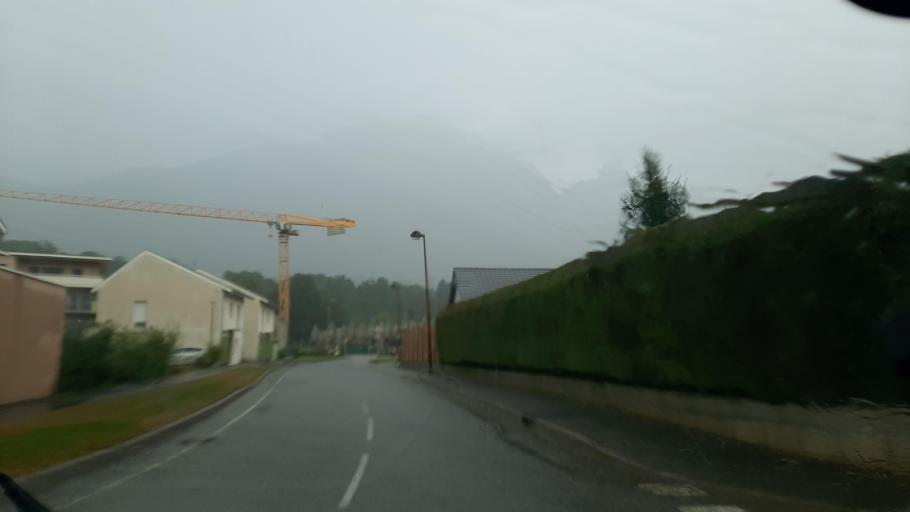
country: FR
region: Rhone-Alpes
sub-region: Departement de la Savoie
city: Gilly-sur-Isere
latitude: 45.6617
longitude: 6.3524
